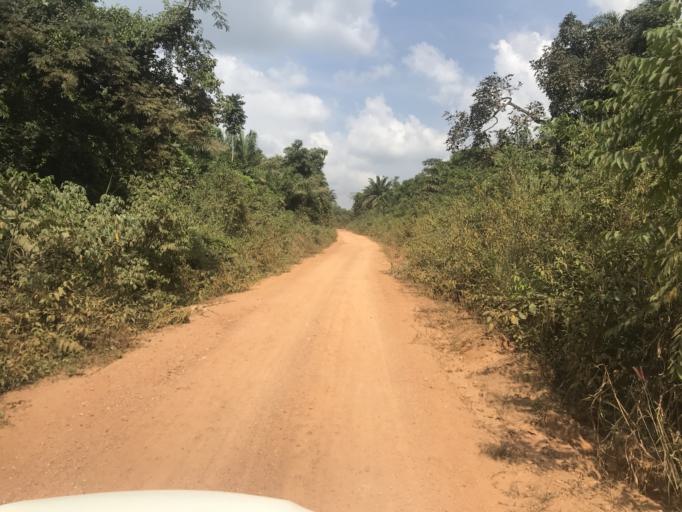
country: NG
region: Osun
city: Inisa
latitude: 7.8840
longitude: 4.3910
